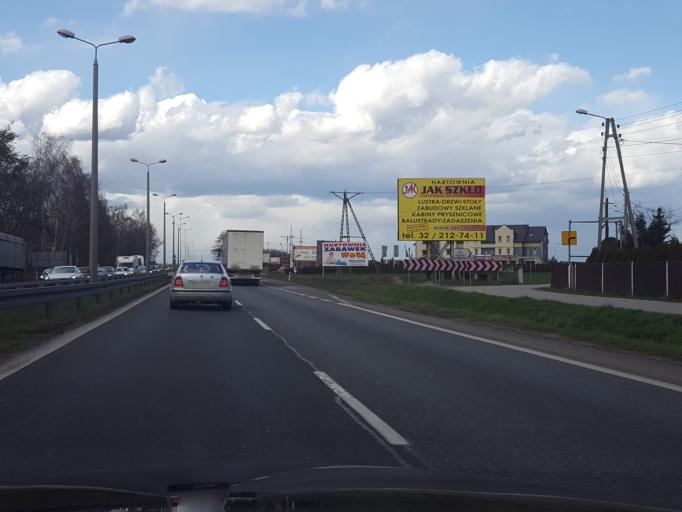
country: PL
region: Silesian Voivodeship
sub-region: Powiat pszczynski
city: Pszczyna
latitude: 49.9904
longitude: 18.9531
